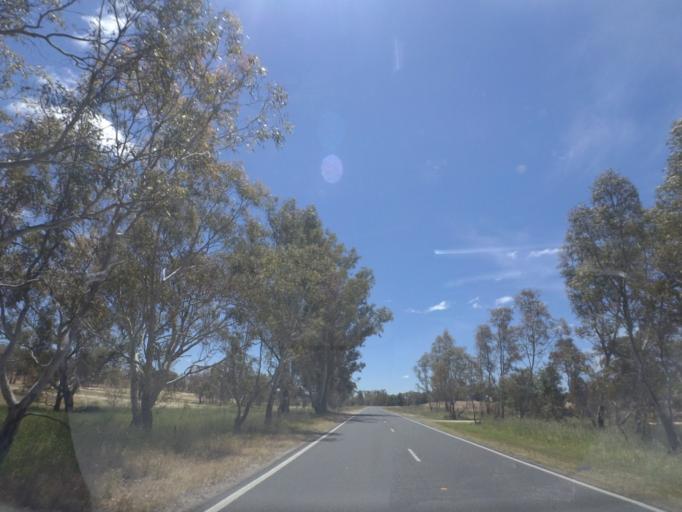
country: AU
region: Victoria
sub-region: Mount Alexander
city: Castlemaine
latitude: -37.1747
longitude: 144.1467
